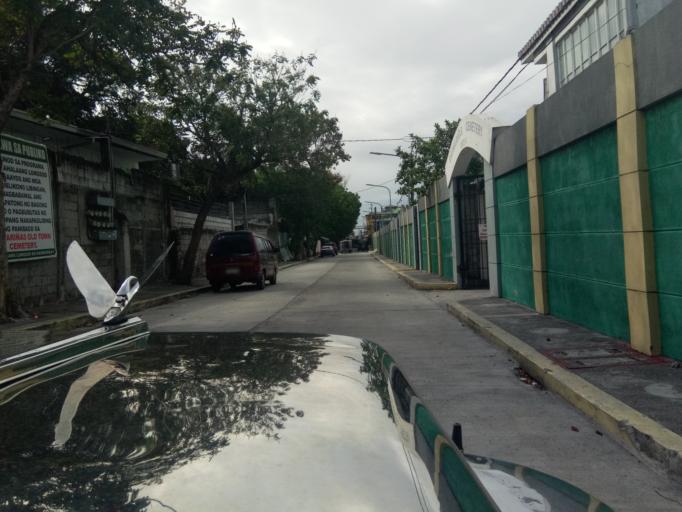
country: PH
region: Calabarzon
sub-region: Province of Cavite
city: Dasmarinas
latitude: 14.3242
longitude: 120.9381
